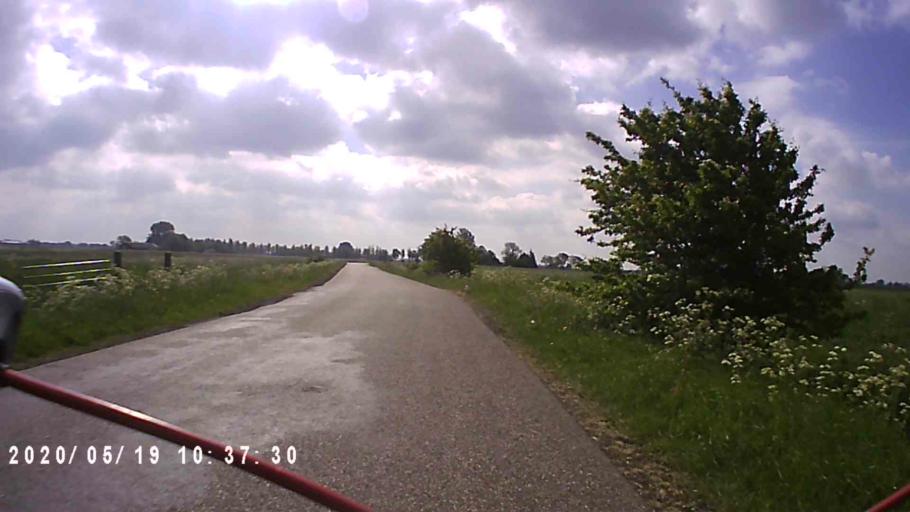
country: NL
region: Friesland
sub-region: Gemeente Kollumerland en Nieuwkruisland
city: Kollum
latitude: 53.2748
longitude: 6.1843
